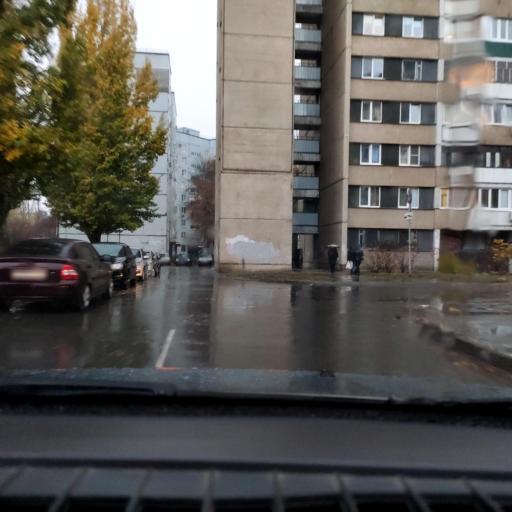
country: RU
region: Samara
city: Tol'yatti
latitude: 53.5299
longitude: 49.3188
